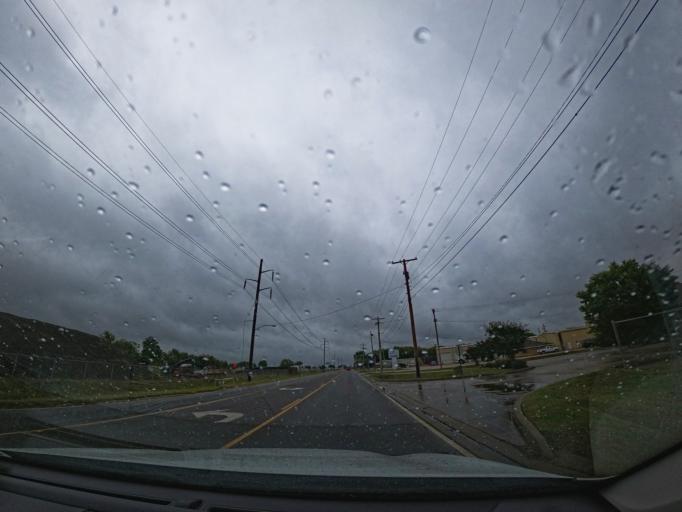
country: US
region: Louisiana
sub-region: Bossier Parish
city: Bossier City
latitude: 32.5245
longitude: -93.6846
